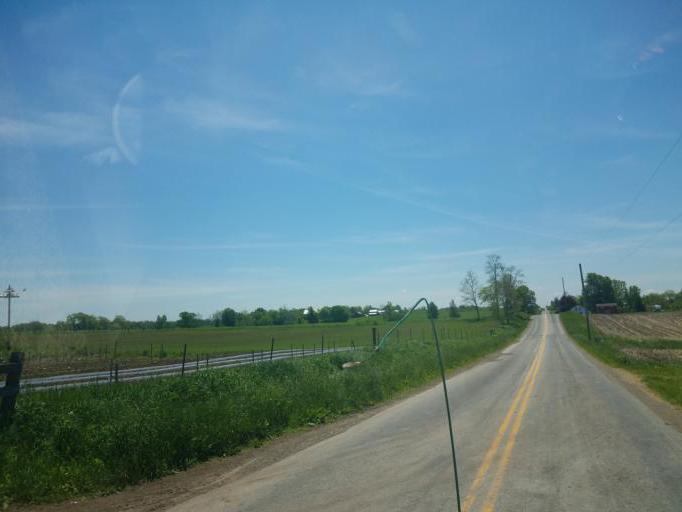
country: US
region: Ohio
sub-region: Ashland County
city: Ashland
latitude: 40.9534
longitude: -82.2437
